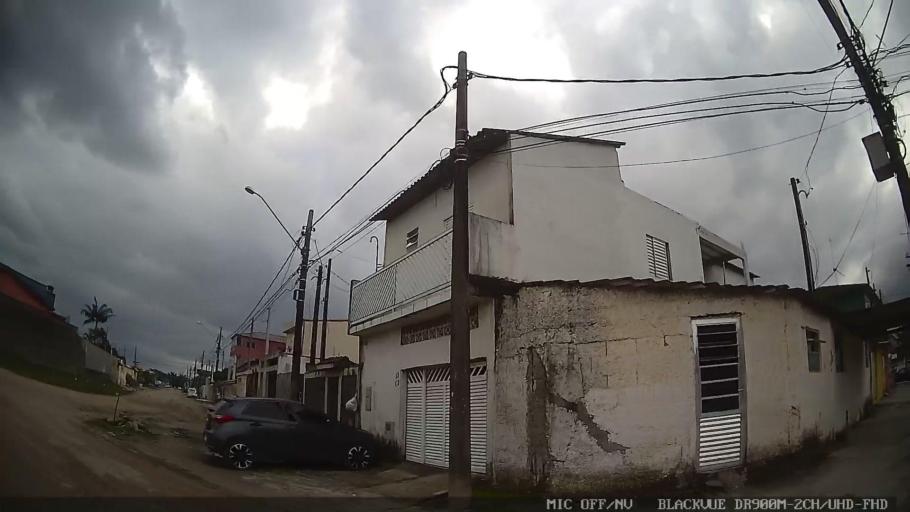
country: BR
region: Sao Paulo
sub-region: Guaruja
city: Guaruja
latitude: -24.0003
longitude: -46.2774
